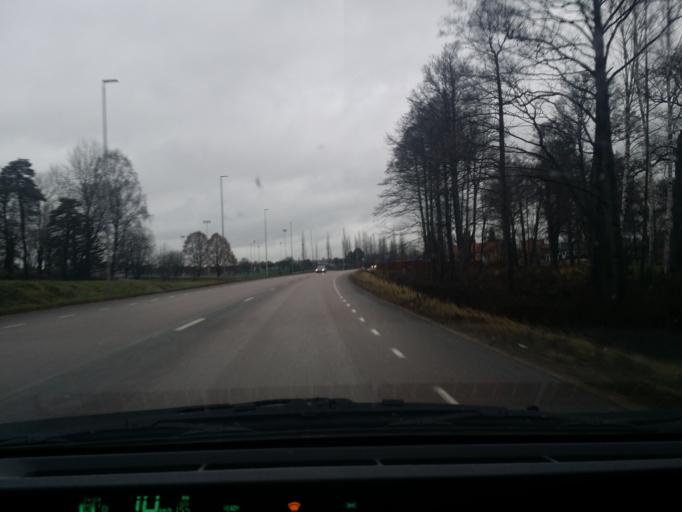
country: SE
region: Vaestmanland
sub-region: Sala Kommun
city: Sala
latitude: 59.9175
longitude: 16.5863
